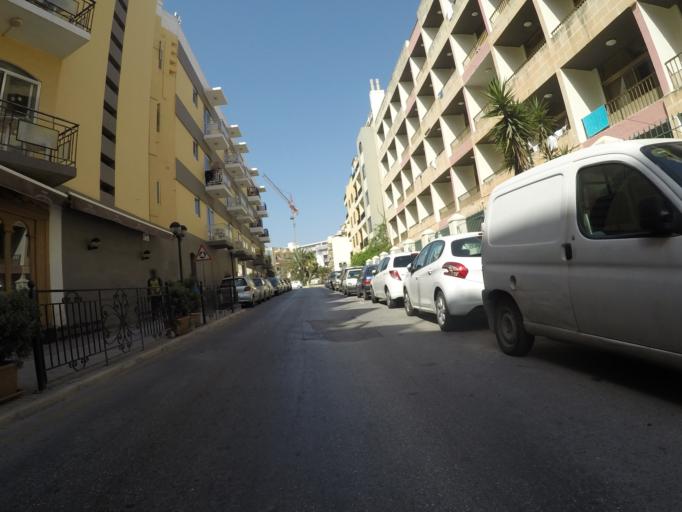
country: MT
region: Saint Paul's Bay
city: San Pawl il-Bahar
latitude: 35.9478
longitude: 14.4102
